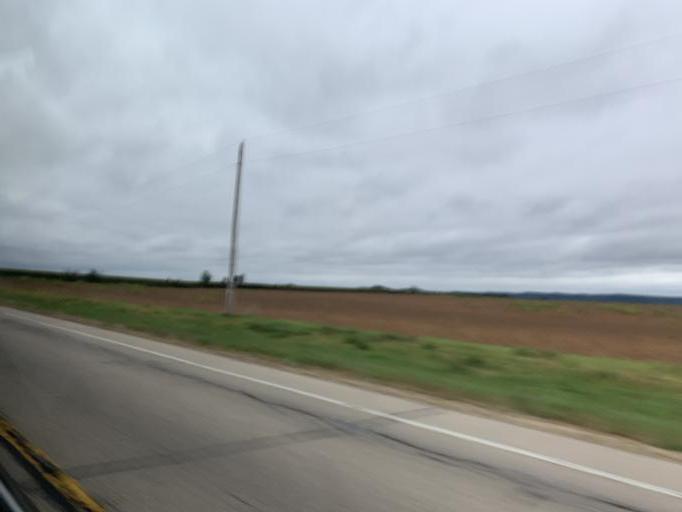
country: US
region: Wisconsin
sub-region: Grant County
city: Muscoda
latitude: 43.2197
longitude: -90.4712
